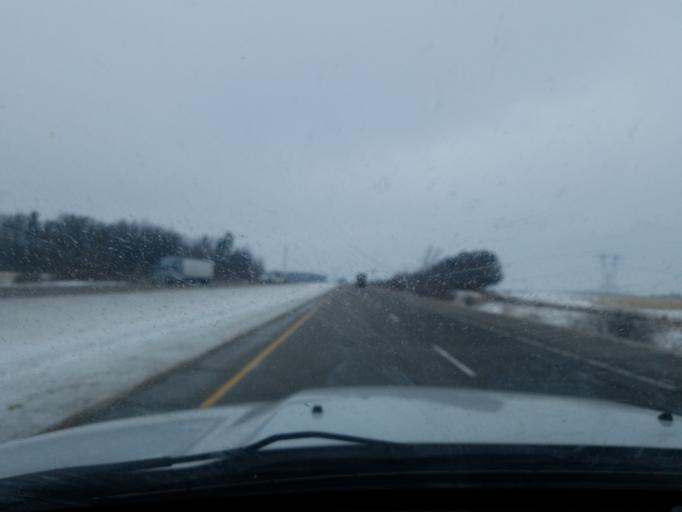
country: US
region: Indiana
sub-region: Marshall County
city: Argos
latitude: 41.1963
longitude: -86.2542
